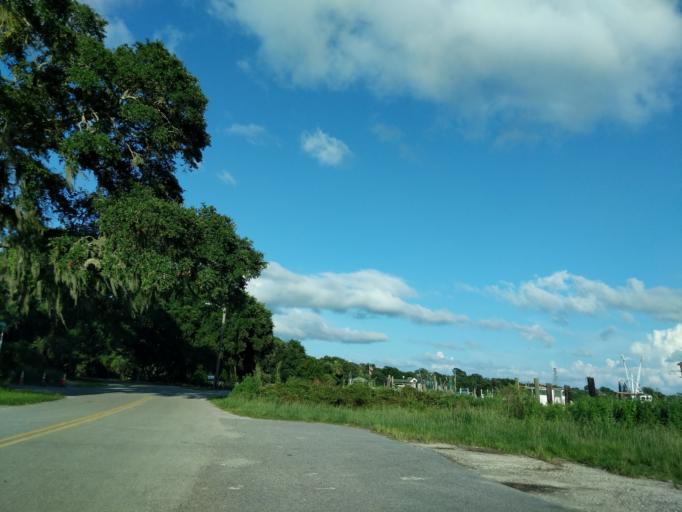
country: US
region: South Carolina
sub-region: Charleston County
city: Awendaw
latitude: 33.0838
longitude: -79.4655
